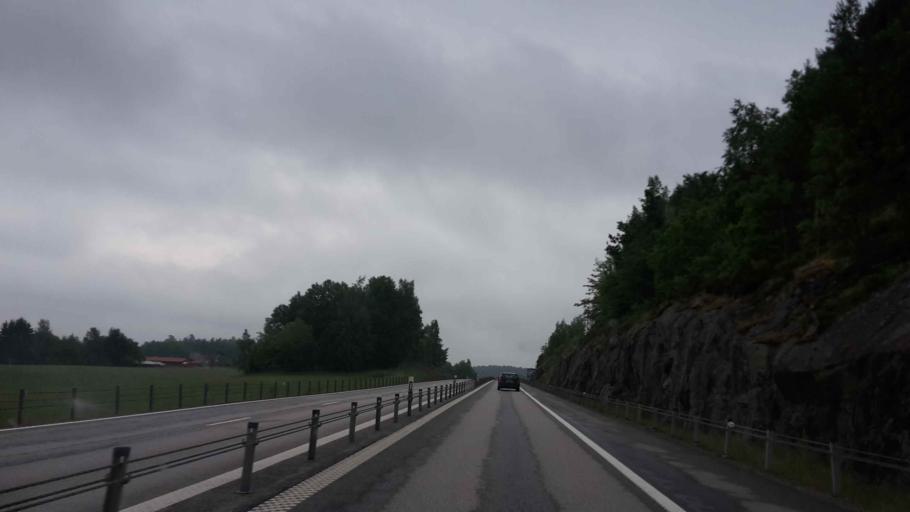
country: SE
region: OEstergoetland
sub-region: Valdemarsviks Kommun
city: Gusum
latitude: 58.2876
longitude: 16.4994
